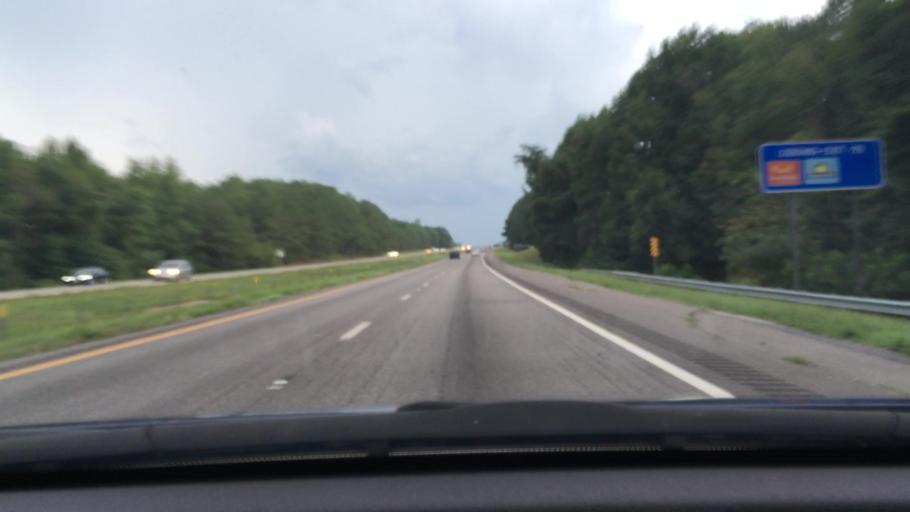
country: US
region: South Carolina
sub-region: Kershaw County
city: Lugoff
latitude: 34.1938
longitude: -80.6763
